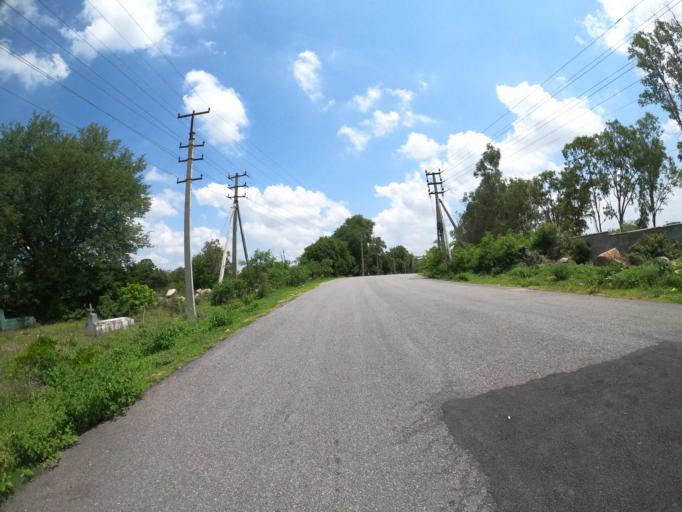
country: IN
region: Telangana
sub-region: Medak
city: Serilingampalle
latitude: 17.3936
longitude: 78.3131
